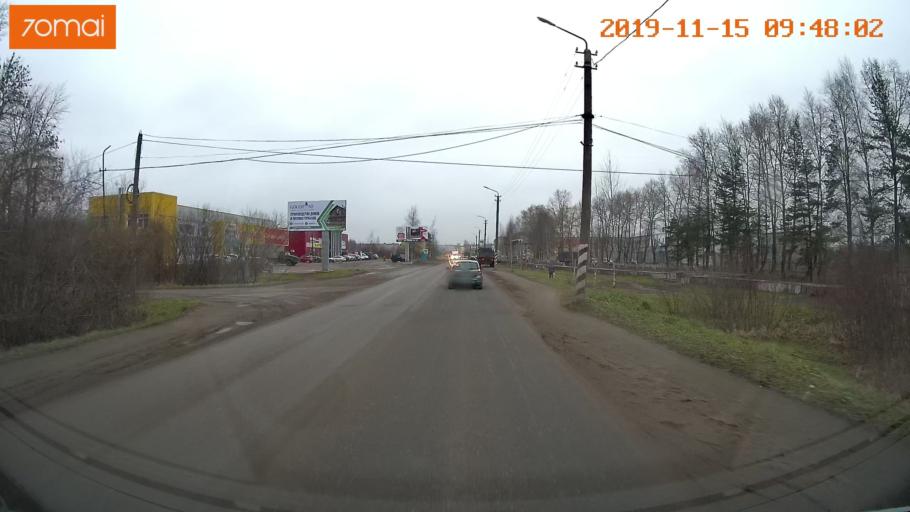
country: RU
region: Vologda
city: Sheksna
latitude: 59.2205
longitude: 38.5118
